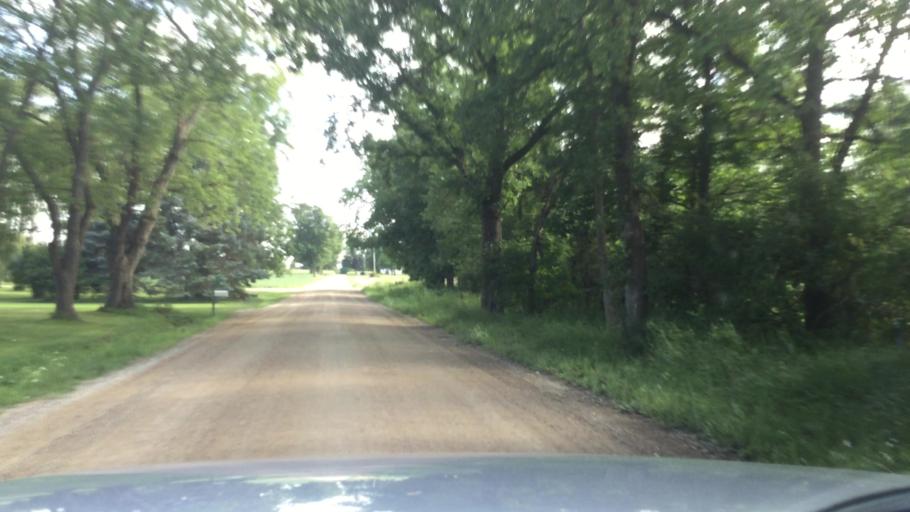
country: US
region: Michigan
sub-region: Ionia County
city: Belding
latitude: 43.0758
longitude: -85.2134
